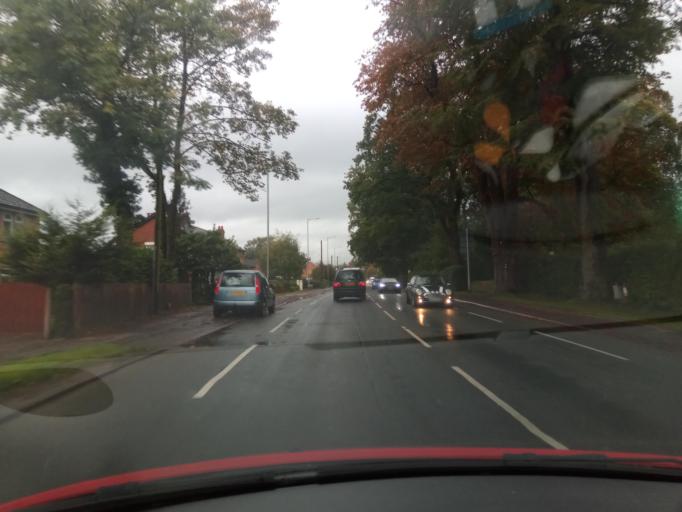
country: GB
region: England
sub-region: Lancashire
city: Catterall
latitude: 53.8553
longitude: -2.7450
